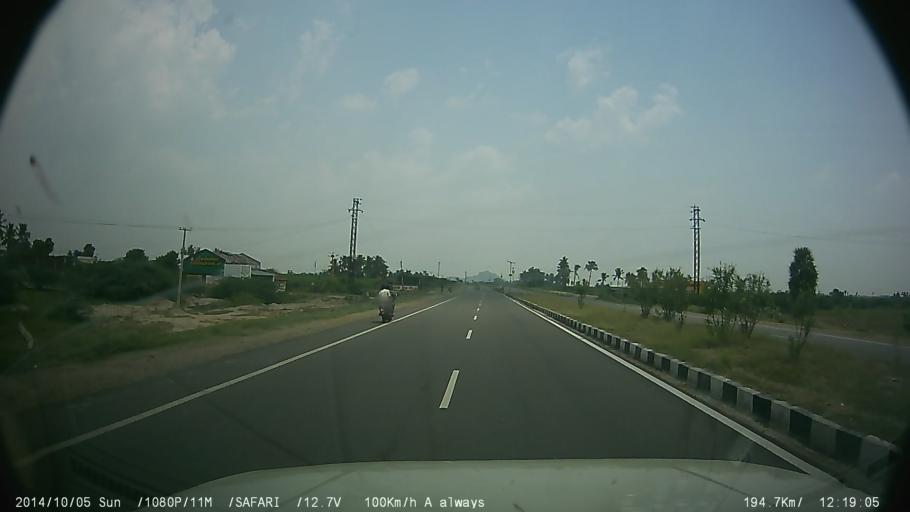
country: IN
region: Tamil Nadu
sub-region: Villupuram
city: Kallakkurichchi
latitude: 11.7348
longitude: 79.0316
